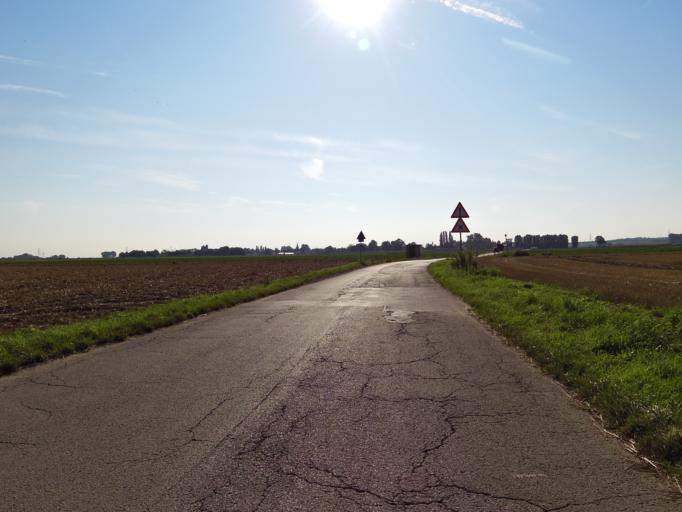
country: DE
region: North Rhine-Westphalia
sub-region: Regierungsbezirk Koln
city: Alsdorf
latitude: 50.8380
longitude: 6.1938
